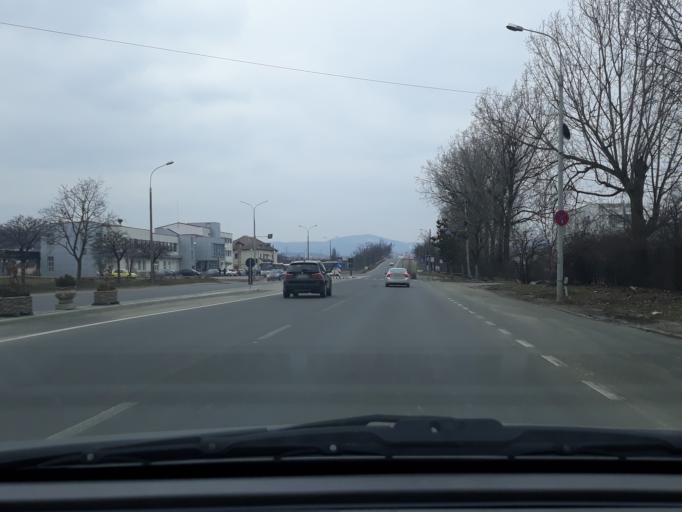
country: RO
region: Salaj
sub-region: Comuna Criseni
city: Criseni
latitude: 47.2219
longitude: 23.0398
